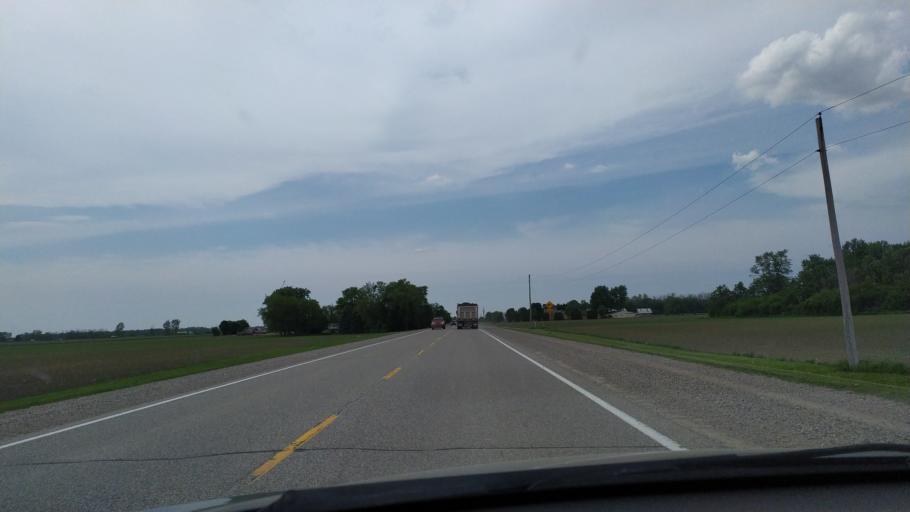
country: CA
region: Ontario
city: Stratford
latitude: 43.2384
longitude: -81.0802
